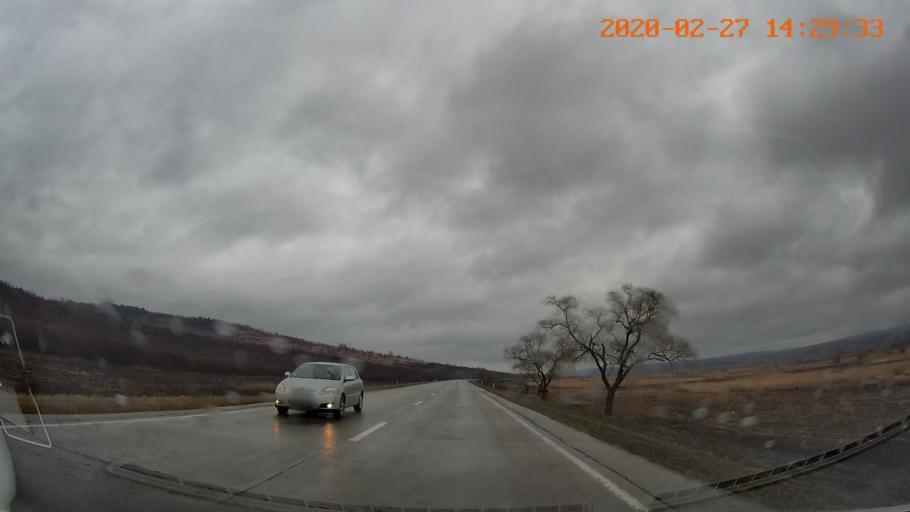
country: MD
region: Taraclia
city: Telenesti
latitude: 47.3887
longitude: 28.4242
